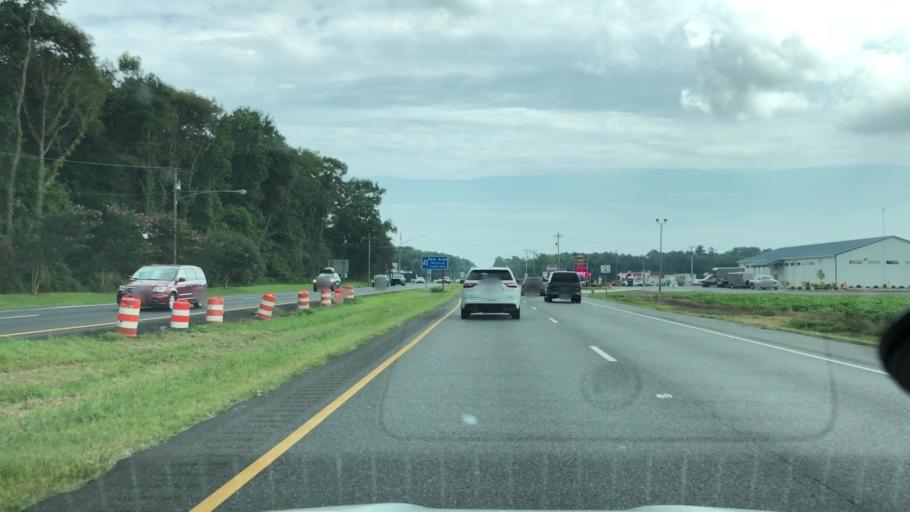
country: US
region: Maryland
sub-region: Worcester County
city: Pocomoke City
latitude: 38.0032
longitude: -75.5433
